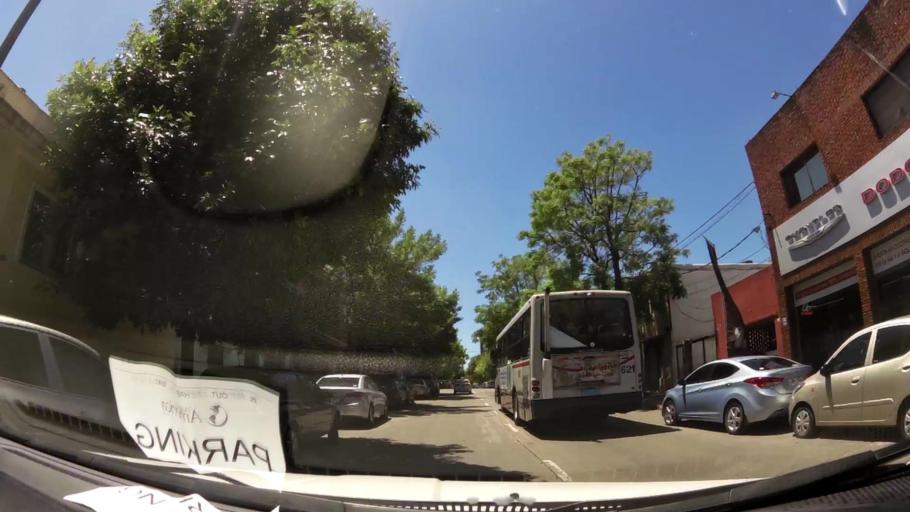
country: UY
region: Montevideo
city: Montevideo
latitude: -34.8920
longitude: -56.1696
